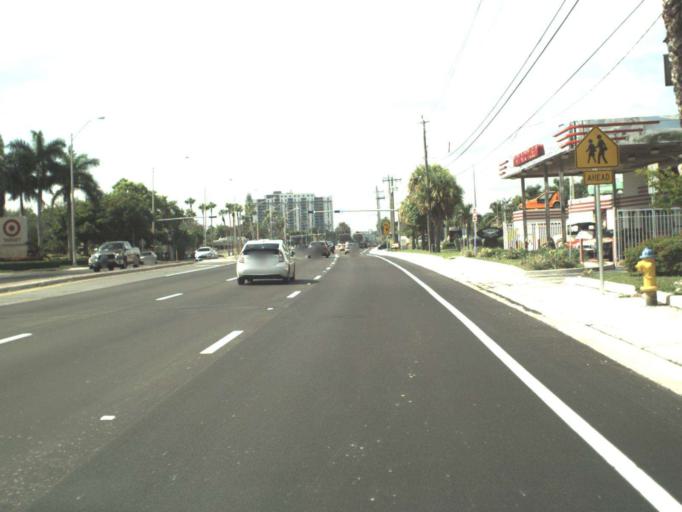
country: US
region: Florida
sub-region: Miami-Dade County
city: North Miami Beach
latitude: 25.9075
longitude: -80.1584
